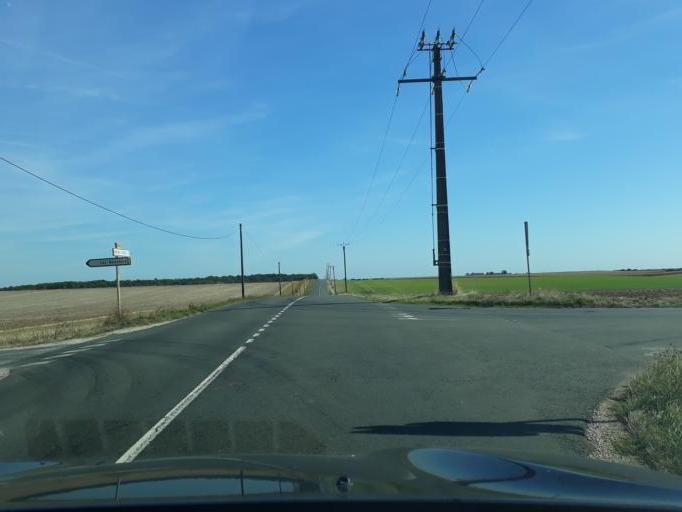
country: FR
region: Centre
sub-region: Departement du Loir-et-Cher
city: Ouzouer-le-Marche
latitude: 47.8743
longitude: 1.5686
